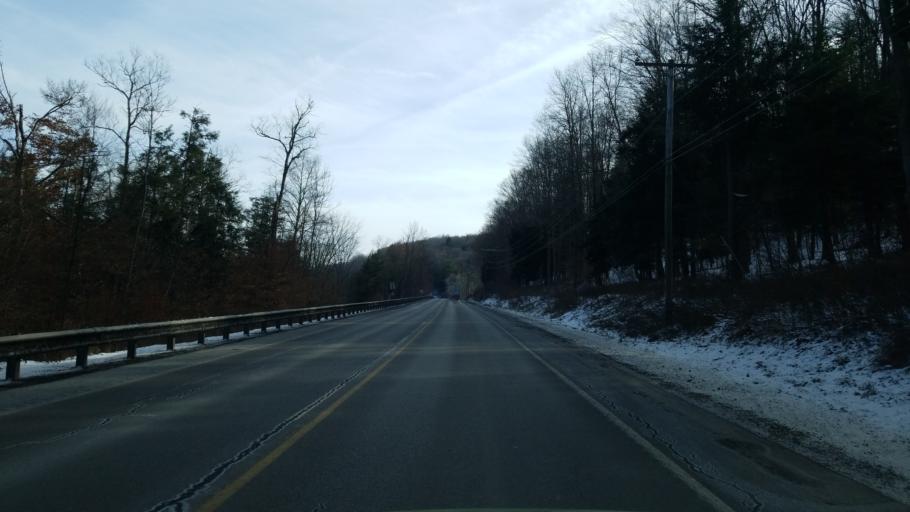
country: US
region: Pennsylvania
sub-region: Clearfield County
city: Treasure Lake
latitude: 41.2028
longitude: -78.5657
